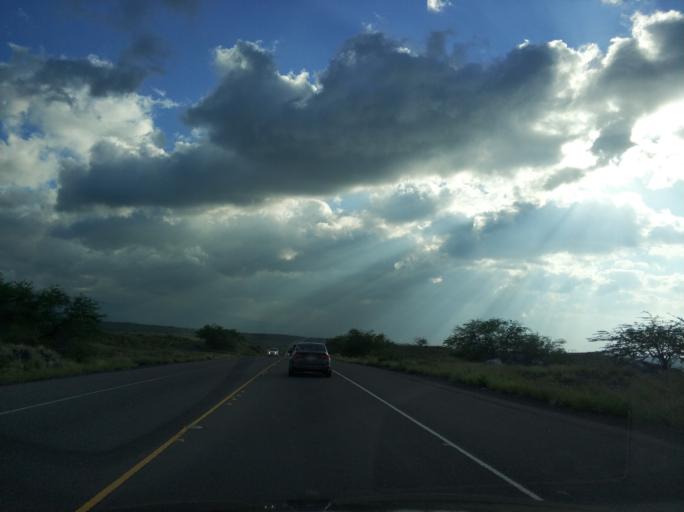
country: US
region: Hawaii
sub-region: Hawaii County
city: Waikoloa Village
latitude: 19.9556
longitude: -155.8268
